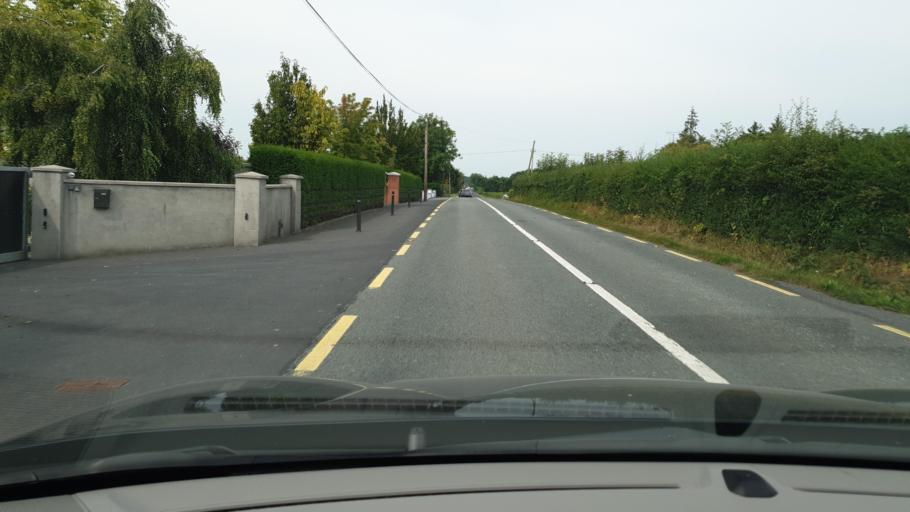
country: IE
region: Leinster
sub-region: An Mhi
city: Trim
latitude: 53.6324
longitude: -6.8042
